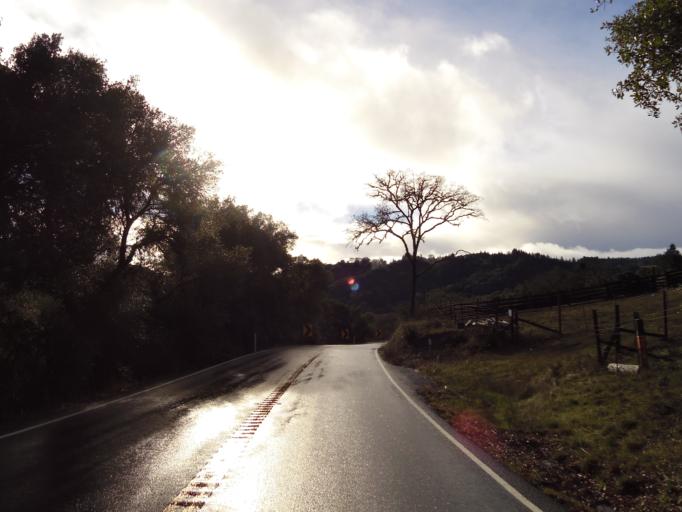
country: US
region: California
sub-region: Sonoma County
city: Cloverdale
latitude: 38.8849
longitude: -123.1309
